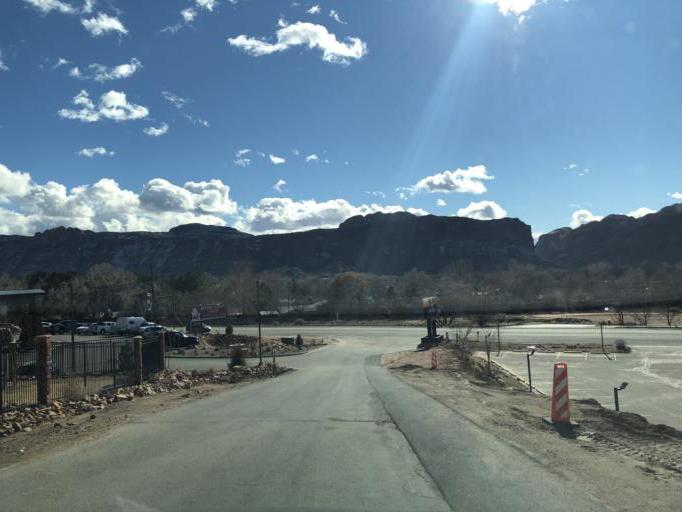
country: US
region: Utah
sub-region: Grand County
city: Moab
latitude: 38.5878
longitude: -109.5581
